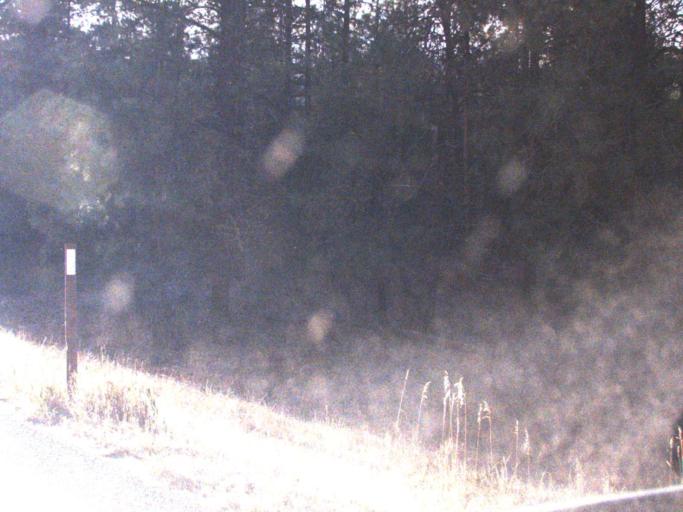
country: US
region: Washington
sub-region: Stevens County
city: Kettle Falls
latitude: 48.8095
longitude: -117.9952
